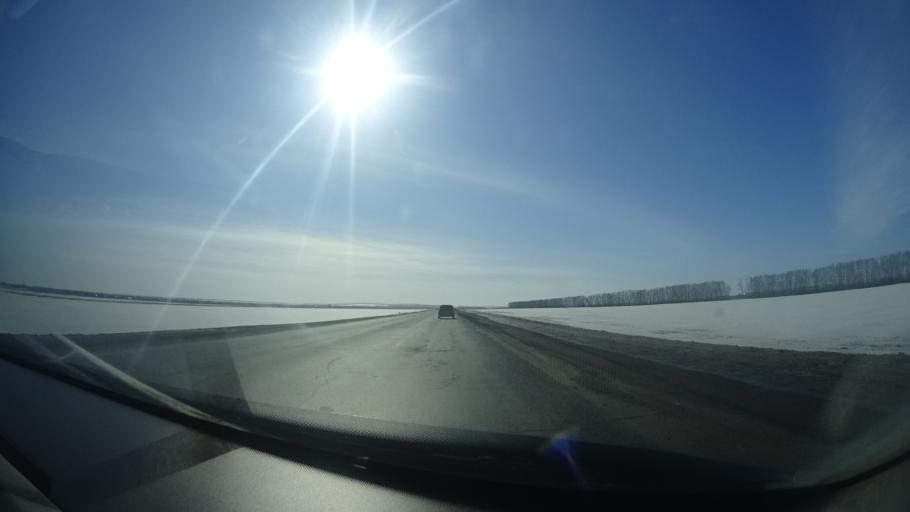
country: RU
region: Bashkortostan
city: Mikhaylovka
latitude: 54.9447
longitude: 55.7500
